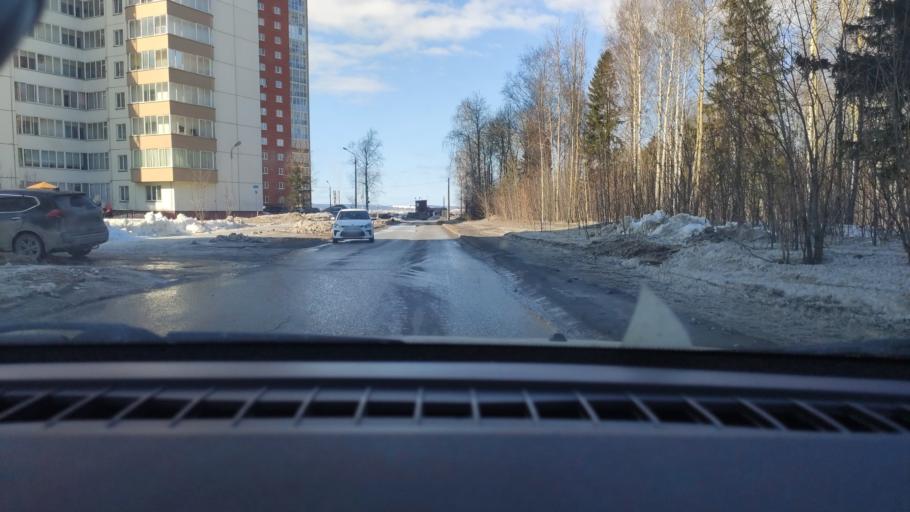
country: RU
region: Perm
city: Polazna
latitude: 58.1345
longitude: 56.4019
